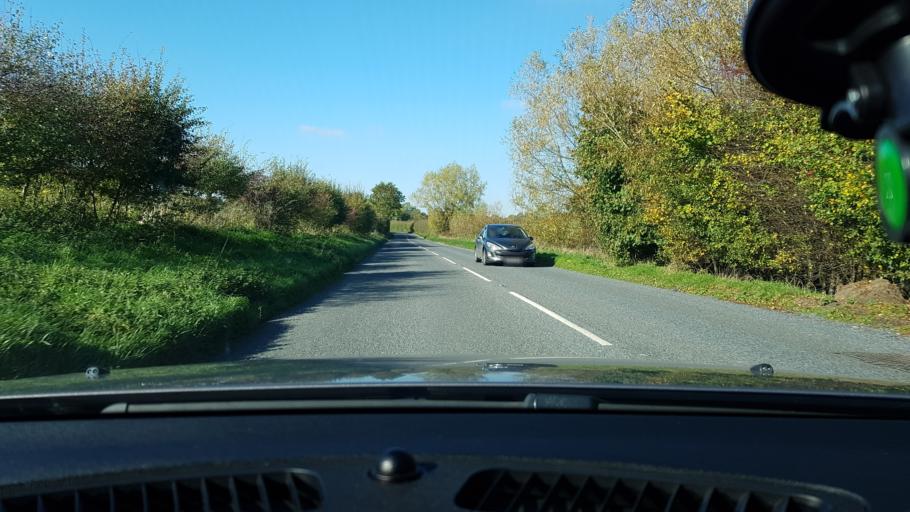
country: GB
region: England
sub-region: Wiltshire
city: Aldbourne
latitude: 51.4674
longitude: -1.6049
